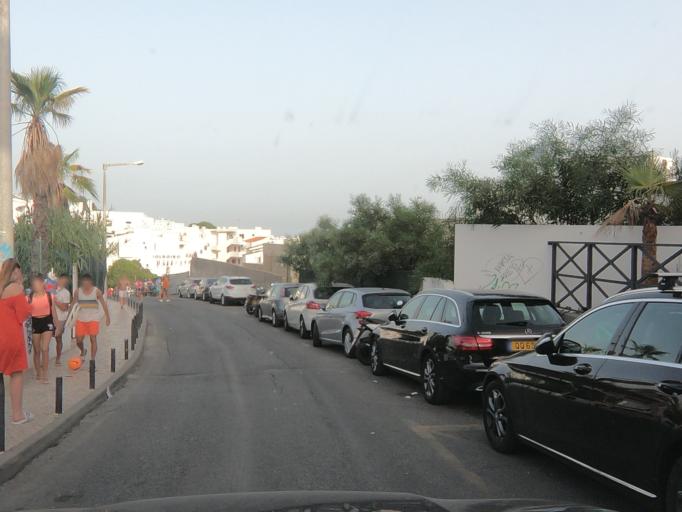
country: PT
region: Faro
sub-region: Albufeira
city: Albufeira
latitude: 37.0884
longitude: -8.2271
